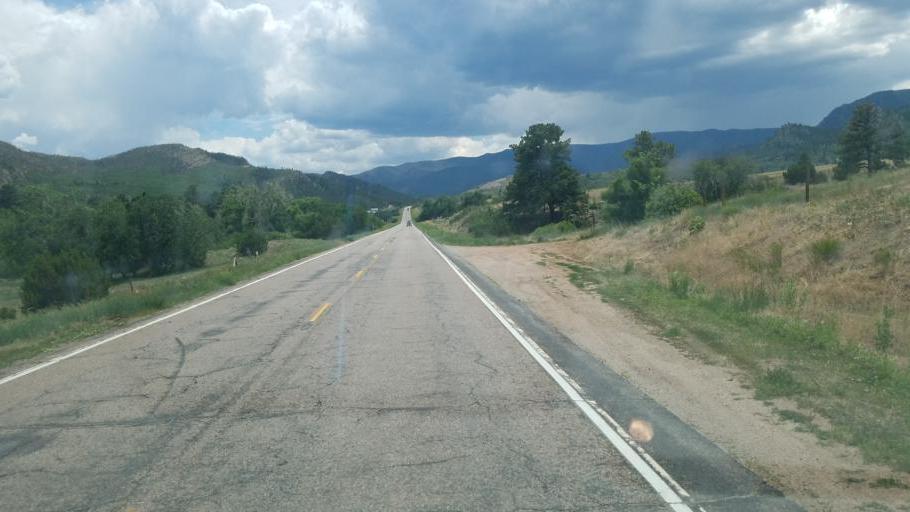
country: US
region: Colorado
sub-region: Fremont County
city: Florence
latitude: 38.2238
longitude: -105.0920
